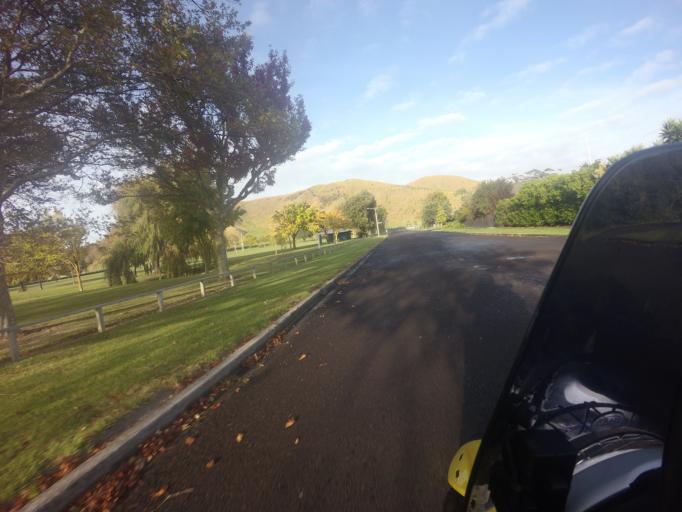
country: NZ
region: Gisborne
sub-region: Gisborne District
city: Gisborne
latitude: -38.6830
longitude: 178.0541
